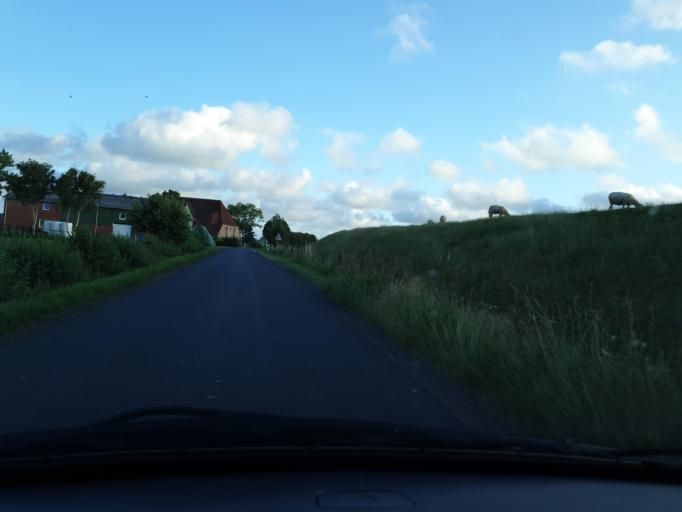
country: DE
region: Schleswig-Holstein
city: Elpersbuttel
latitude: 54.0791
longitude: 9.0264
